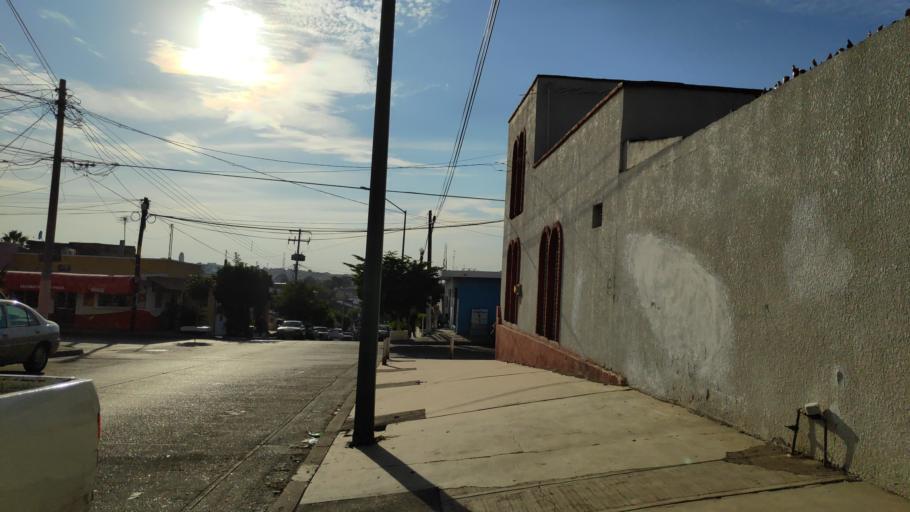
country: MX
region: Sinaloa
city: Culiacan
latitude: 24.7913
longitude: -107.4061
